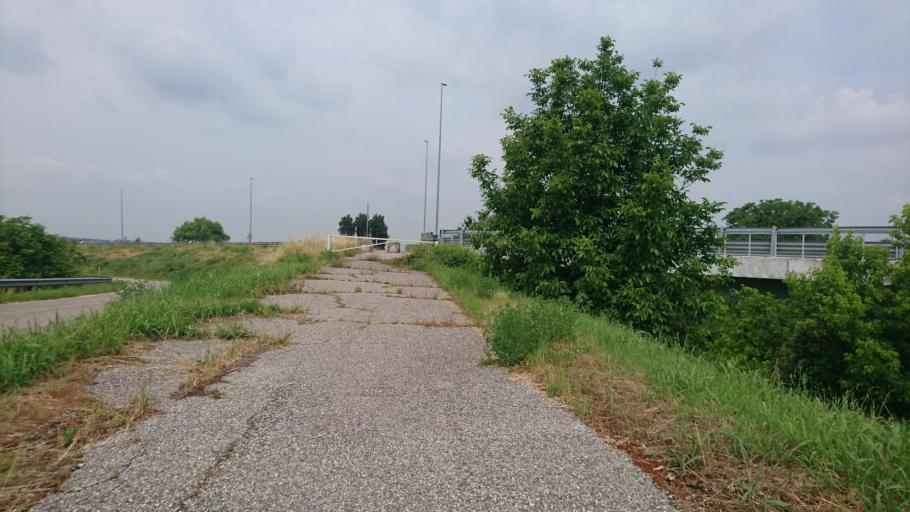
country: IT
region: Veneto
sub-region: Provincia di Padova
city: Vighizzolo d'Este
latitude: 45.1412
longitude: 11.6345
